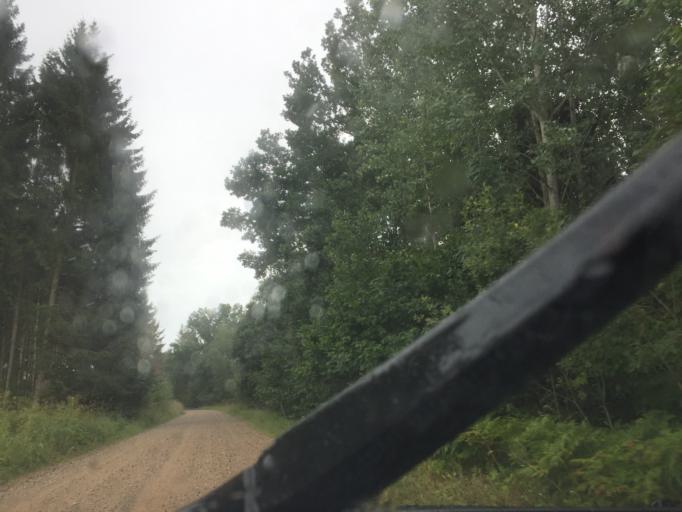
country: LV
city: Tervete
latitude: 56.3747
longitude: 23.4573
